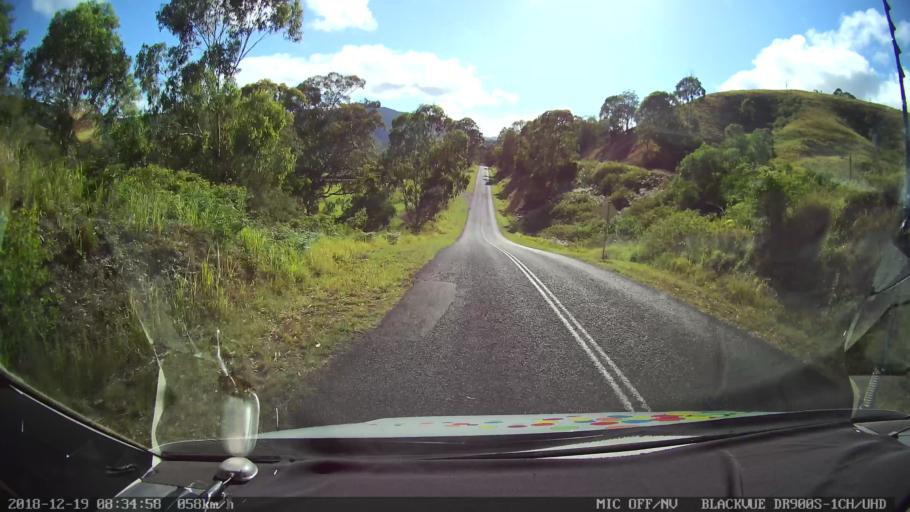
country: AU
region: New South Wales
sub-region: Kyogle
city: Kyogle
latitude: -28.3219
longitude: 152.9648
